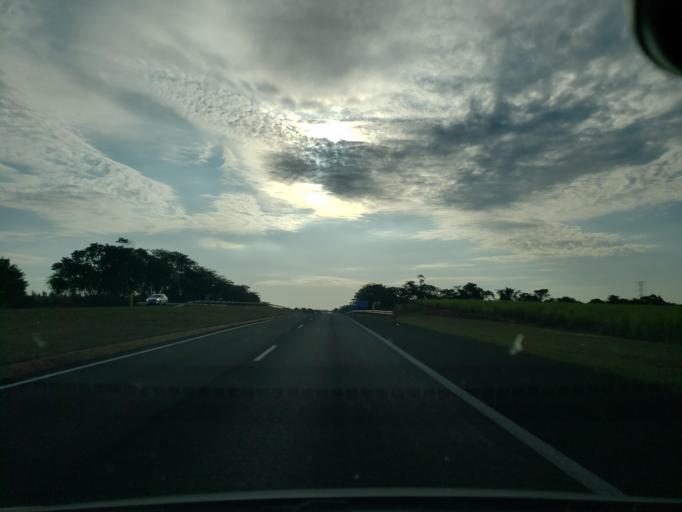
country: BR
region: Sao Paulo
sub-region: Mirandopolis
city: Mirandopolis
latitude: -21.0947
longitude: -51.0492
